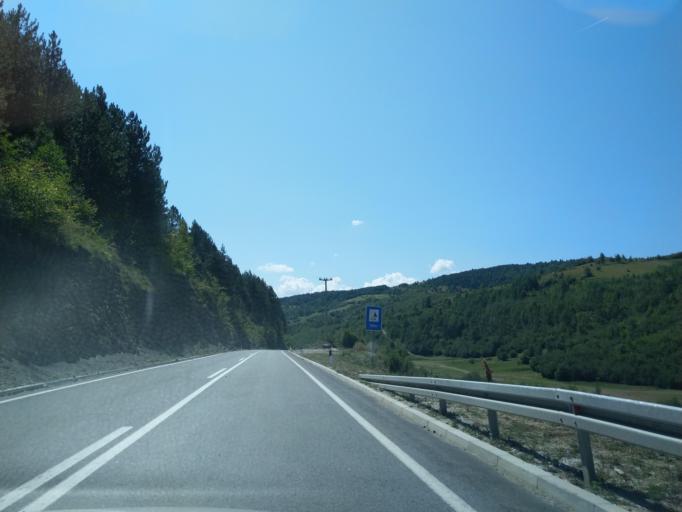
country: RS
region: Central Serbia
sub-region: Zlatiborski Okrug
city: Sjenica
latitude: 43.2911
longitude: 19.9416
